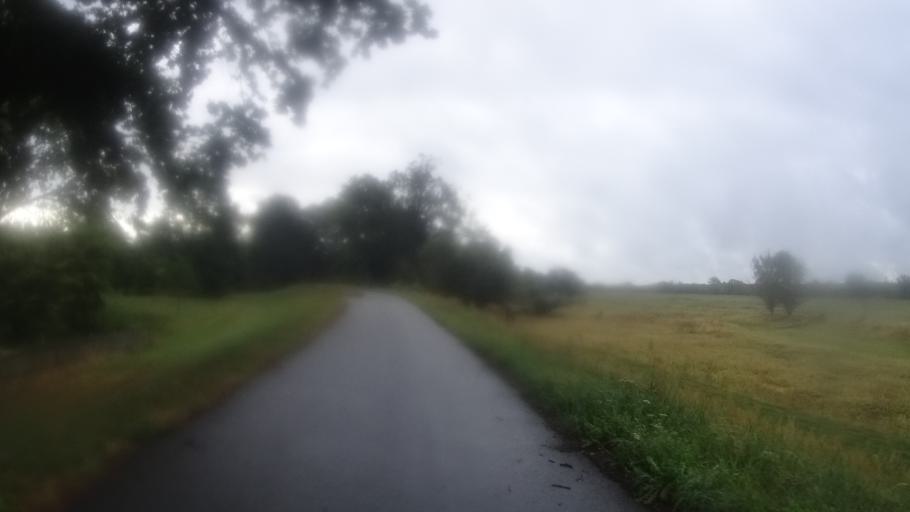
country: DE
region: Lower Saxony
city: Gorleben
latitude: 53.0706
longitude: 11.3261
